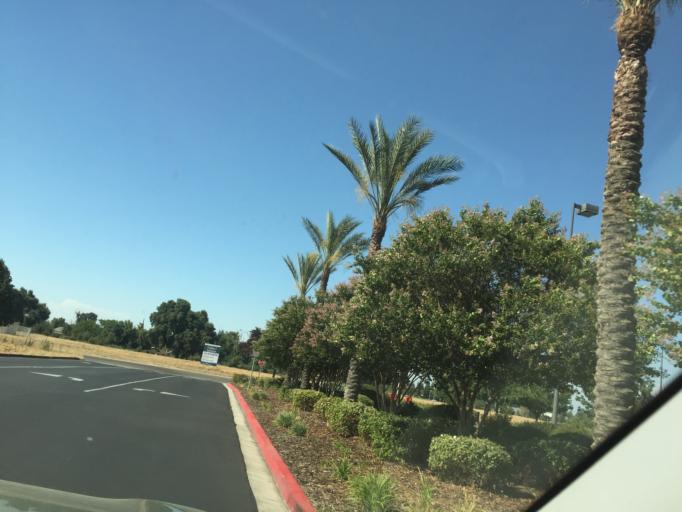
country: US
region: California
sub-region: Tulare County
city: Visalia
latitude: 36.2936
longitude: -119.3077
